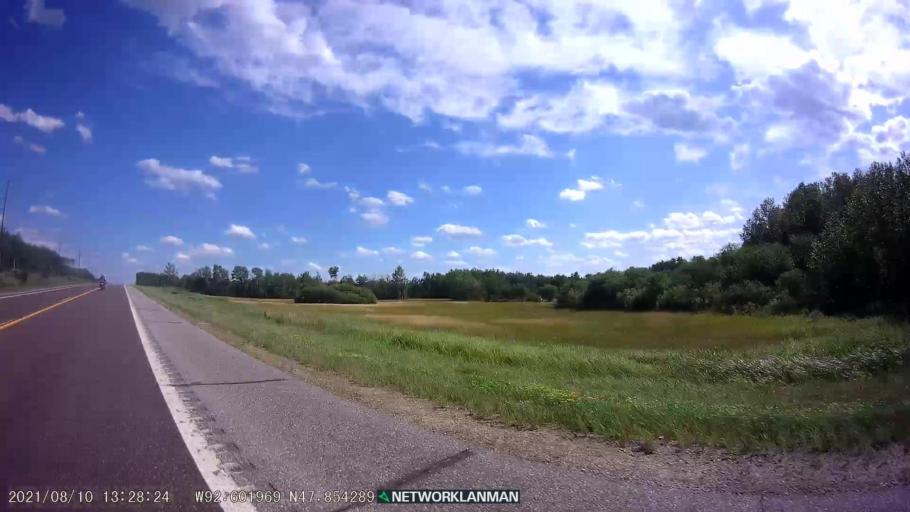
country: US
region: Minnesota
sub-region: Saint Louis County
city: Mountain Iron
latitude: 47.8541
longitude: -92.6017
